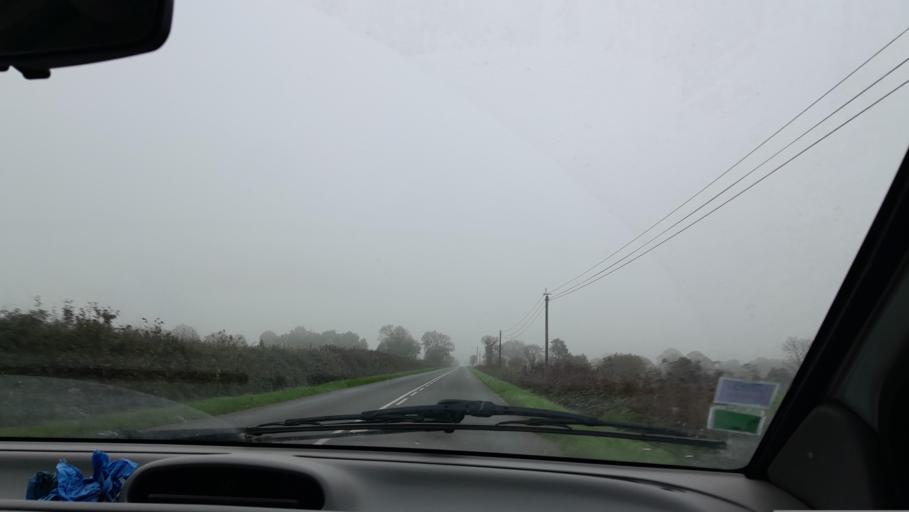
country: FR
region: Pays de la Loire
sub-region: Departement de la Mayenne
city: Ahuille
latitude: 48.0312
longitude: -0.9076
